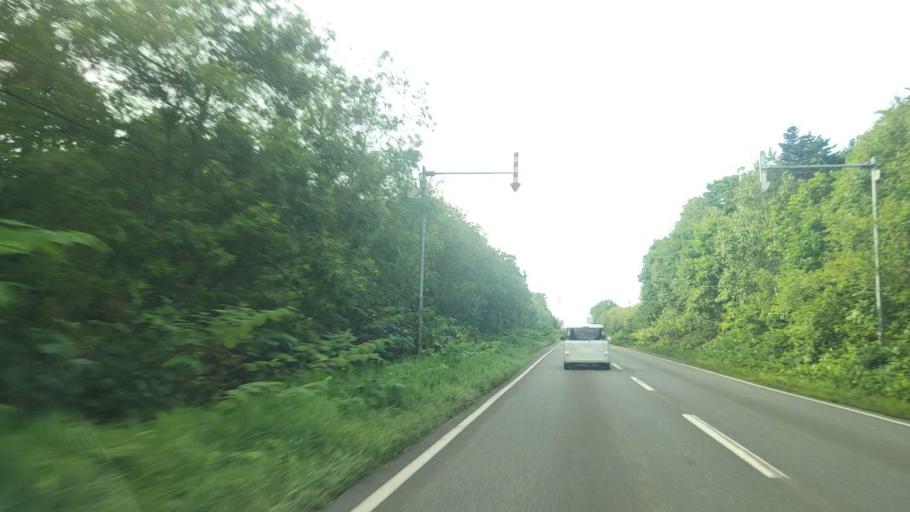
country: JP
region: Hokkaido
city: Makubetsu
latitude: 45.0507
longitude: 141.7510
